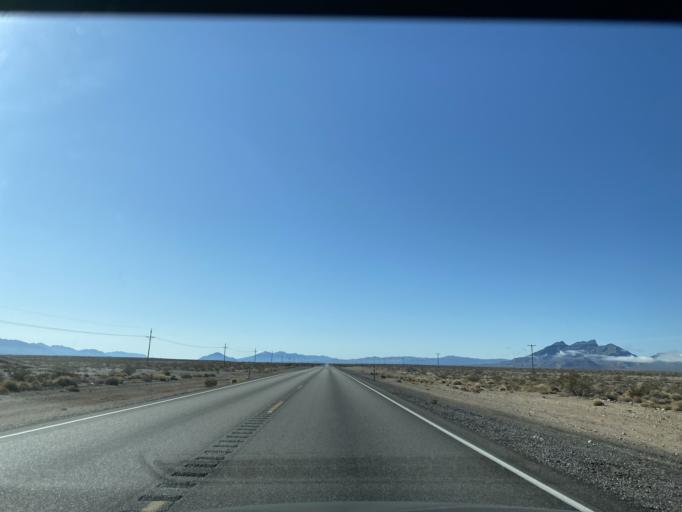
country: US
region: Nevada
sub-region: Nye County
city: Pahrump
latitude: 36.4794
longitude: -116.4216
